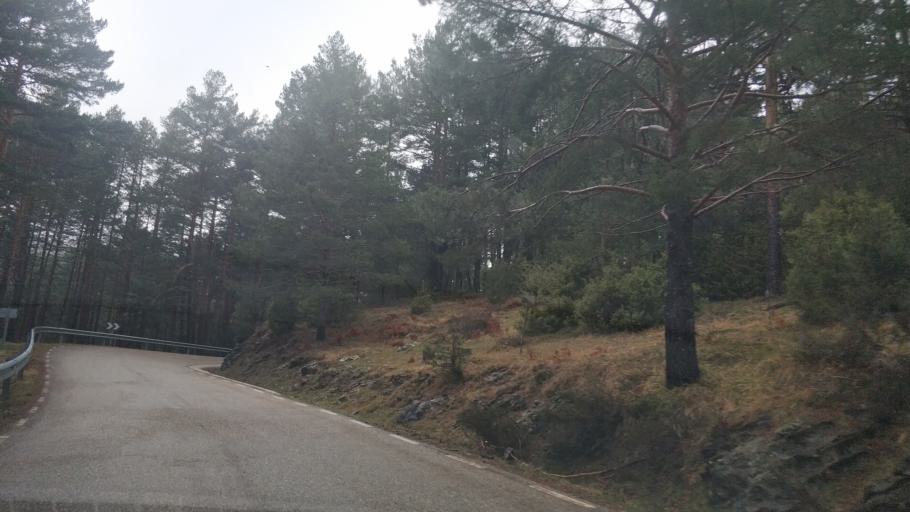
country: ES
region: Castille and Leon
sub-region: Provincia de Burgos
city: Neila
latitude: 42.0400
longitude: -3.0063
